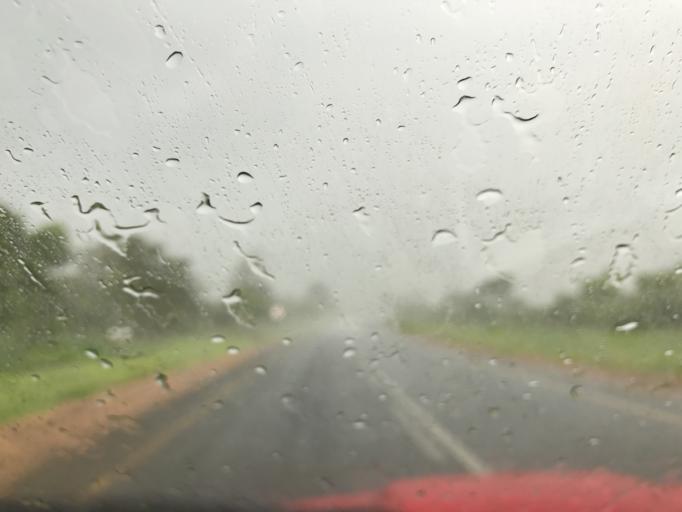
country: MZ
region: Nampula
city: Nampula
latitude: -15.0041
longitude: 38.5092
